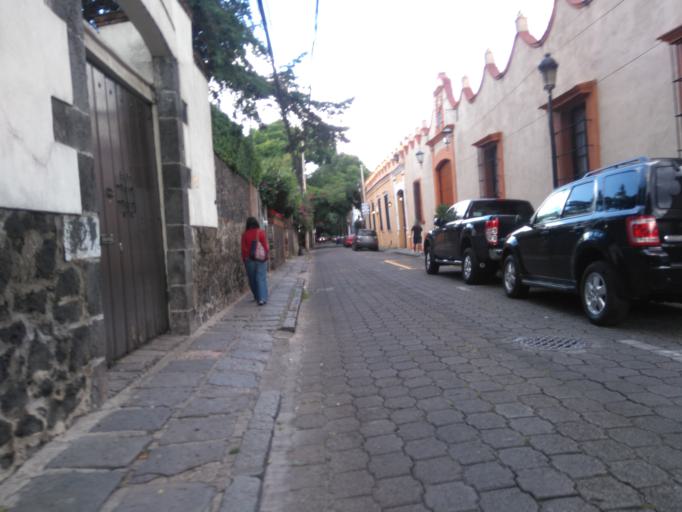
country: MX
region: Mexico City
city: Coyoacan
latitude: 19.3495
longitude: -99.1753
